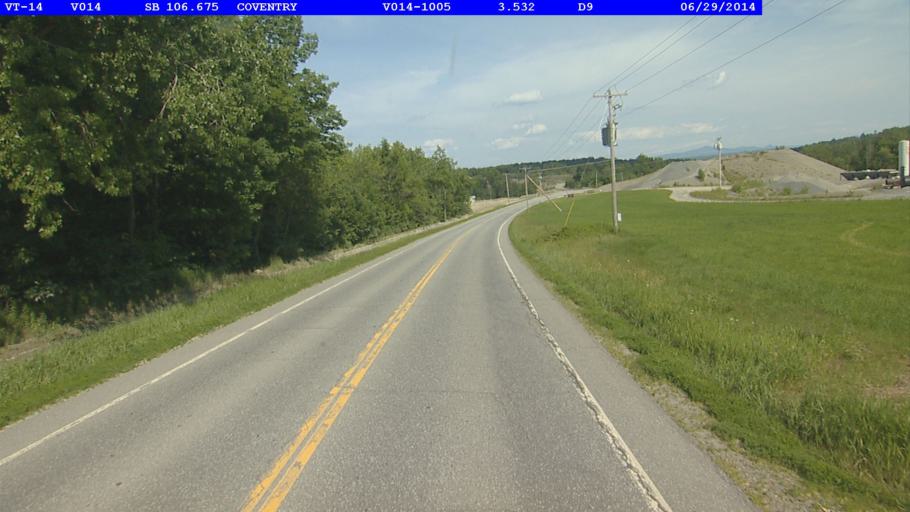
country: US
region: Vermont
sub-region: Orleans County
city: Newport
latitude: 44.9111
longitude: -72.2671
